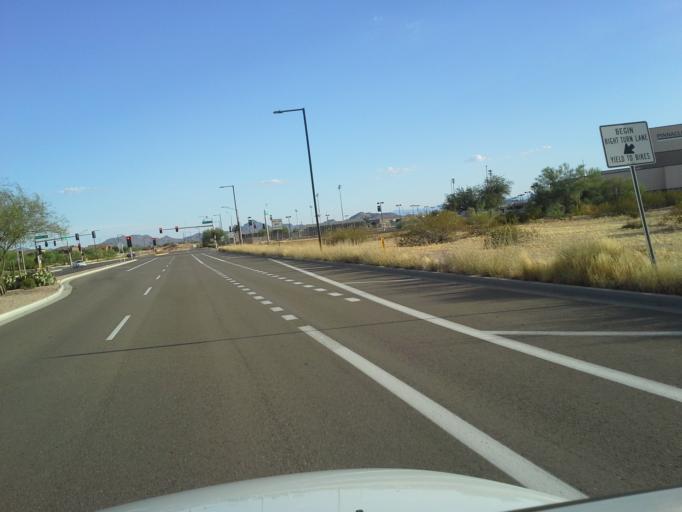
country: US
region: Arizona
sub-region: Maricopa County
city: Cave Creek
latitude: 33.6823
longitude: -112.0052
